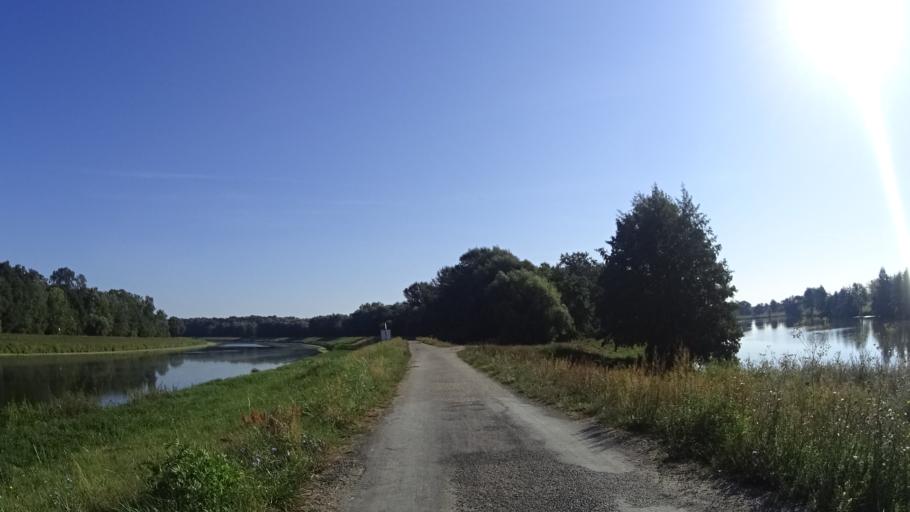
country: CZ
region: South Moravian
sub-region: Okres Breclav
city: Lanzhot
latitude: 48.6889
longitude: 16.9947
